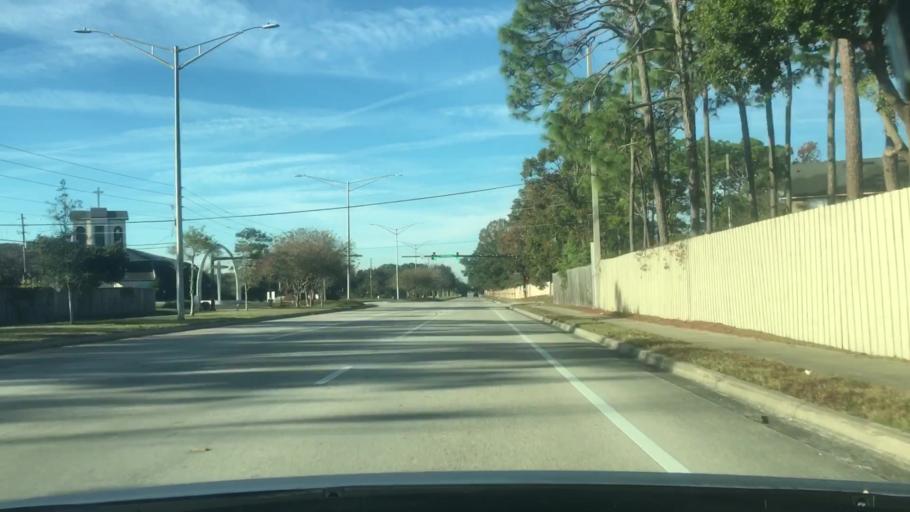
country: US
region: Florida
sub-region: Duval County
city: Atlantic Beach
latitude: 30.3527
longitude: -81.5110
